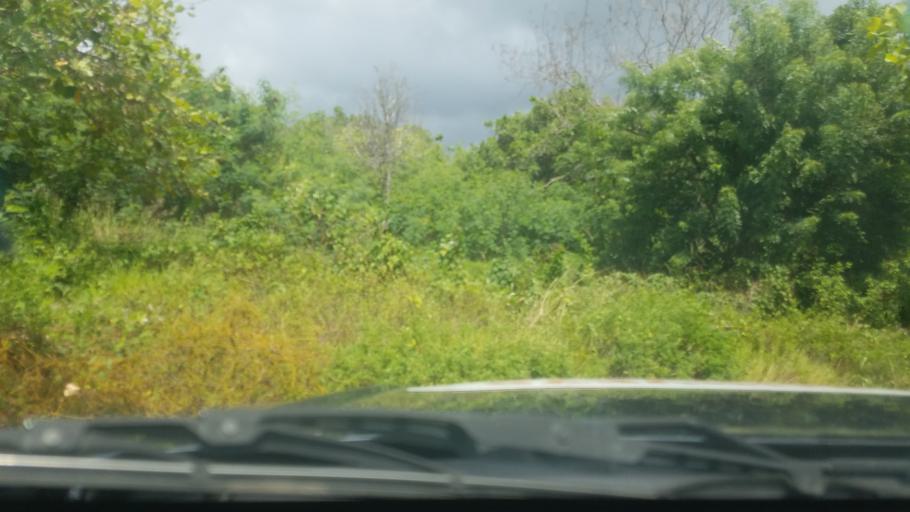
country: LC
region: Praslin
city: Praslin
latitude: 13.8670
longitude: -60.8942
